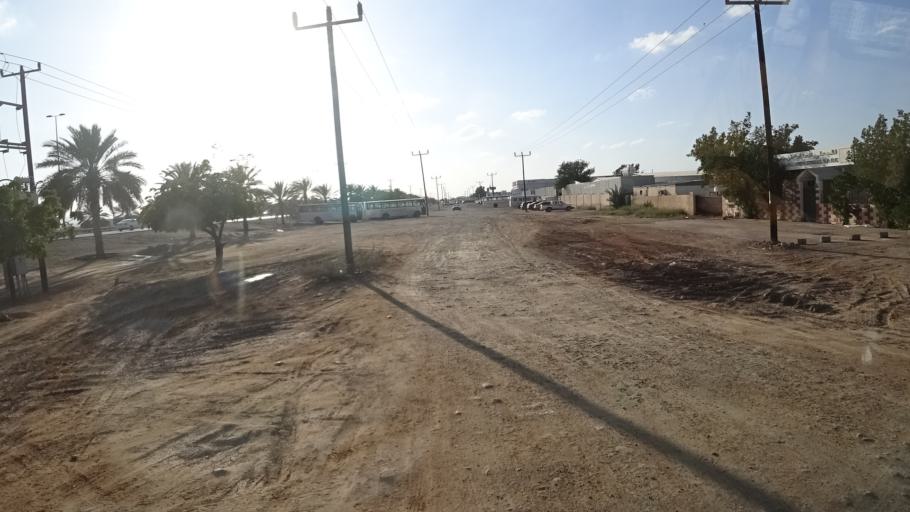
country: OM
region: Muhafazat Masqat
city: As Sib al Jadidah
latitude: 23.5902
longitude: 58.2334
